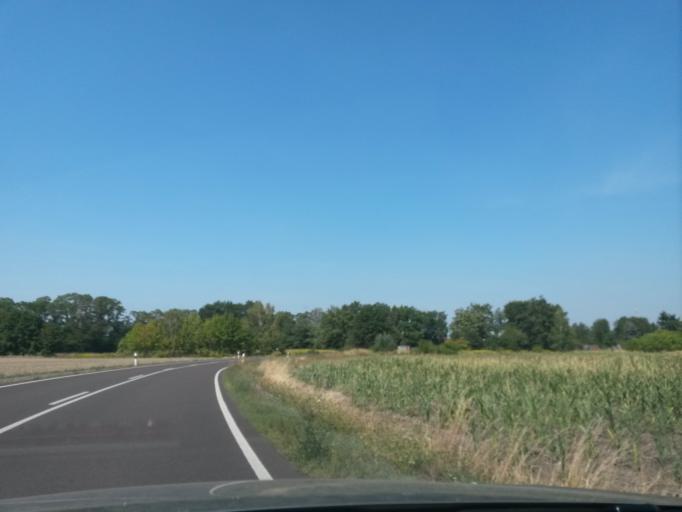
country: DE
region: Brandenburg
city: Ziesar
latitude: 52.2561
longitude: 12.2917
